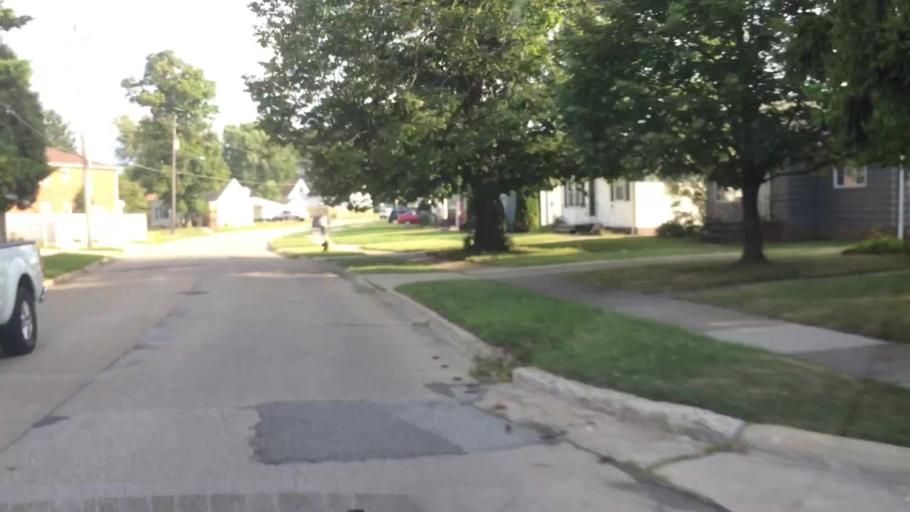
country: US
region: Ohio
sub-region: Cuyahoga County
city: Parma Heights
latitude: 41.3976
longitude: -81.7450
